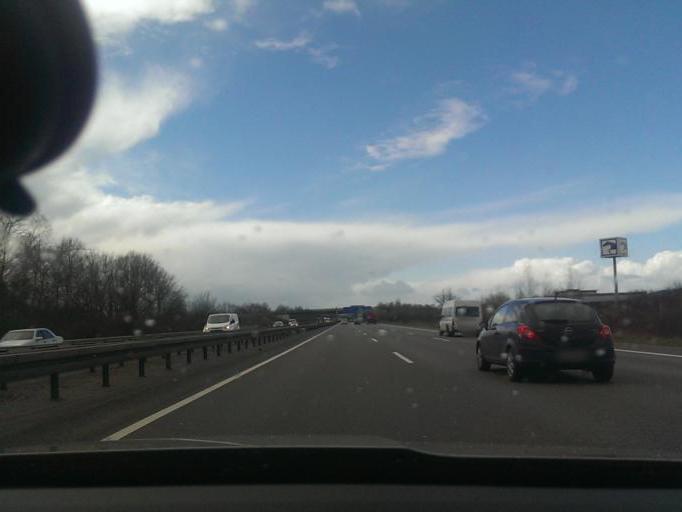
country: DE
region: Lower Saxony
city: Klein Schwulper
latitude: 52.3239
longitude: 10.4781
